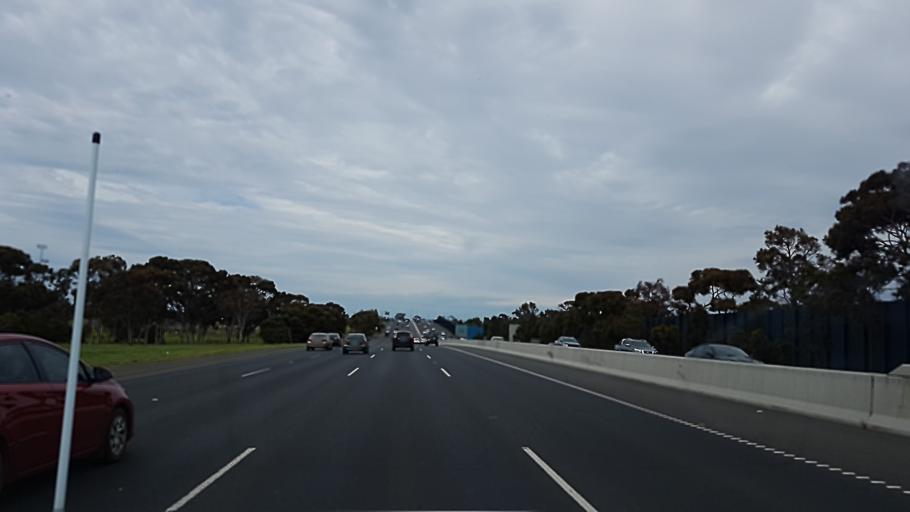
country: AU
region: Victoria
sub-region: Hobsons Bay
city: Laverton
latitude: -37.8561
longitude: 144.7786
